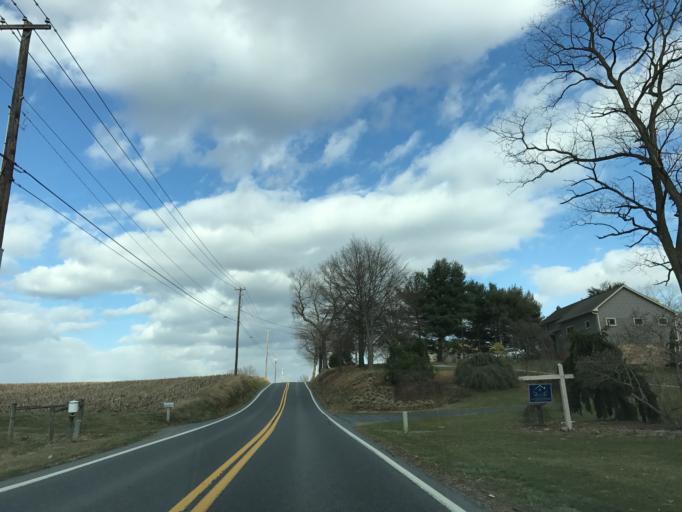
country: US
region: Pennsylvania
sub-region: Lancaster County
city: Elizabethtown
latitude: 40.1697
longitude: -76.5686
